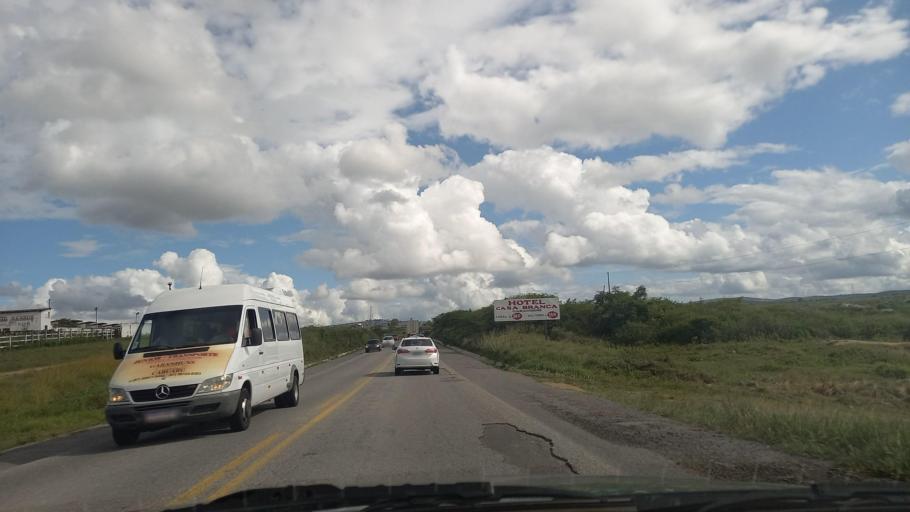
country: BR
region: Pernambuco
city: Garanhuns
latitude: -8.8224
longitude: -36.4491
